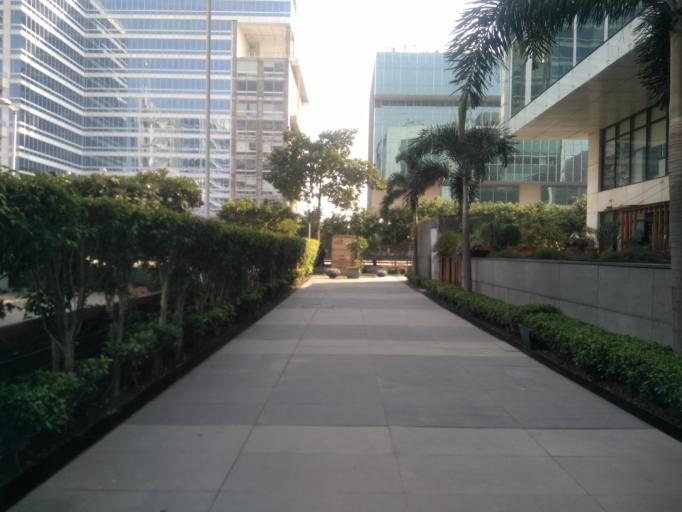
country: IN
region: Uttar Pradesh
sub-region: Gautam Buddha Nagar
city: Noida
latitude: 28.5392
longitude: 77.2887
